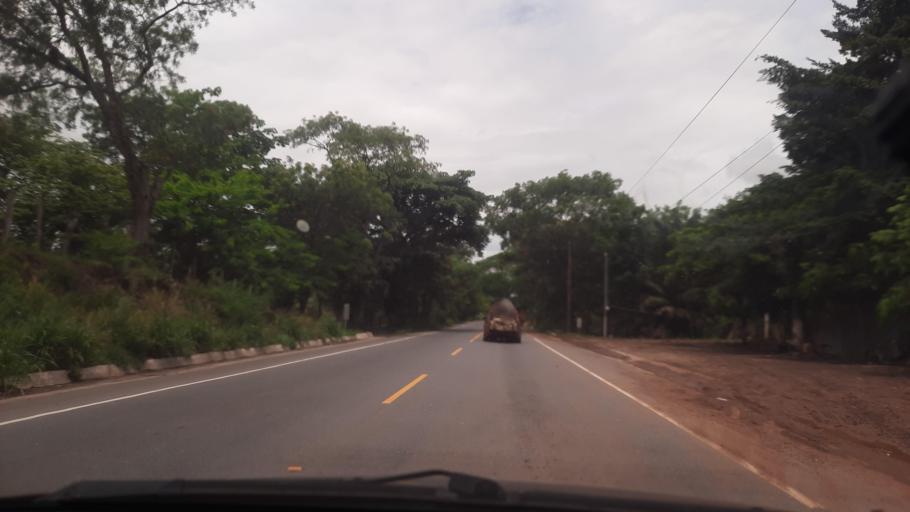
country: GT
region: Zacapa
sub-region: Municipio de Zacapa
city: Gualan
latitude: 15.2092
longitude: -89.2411
